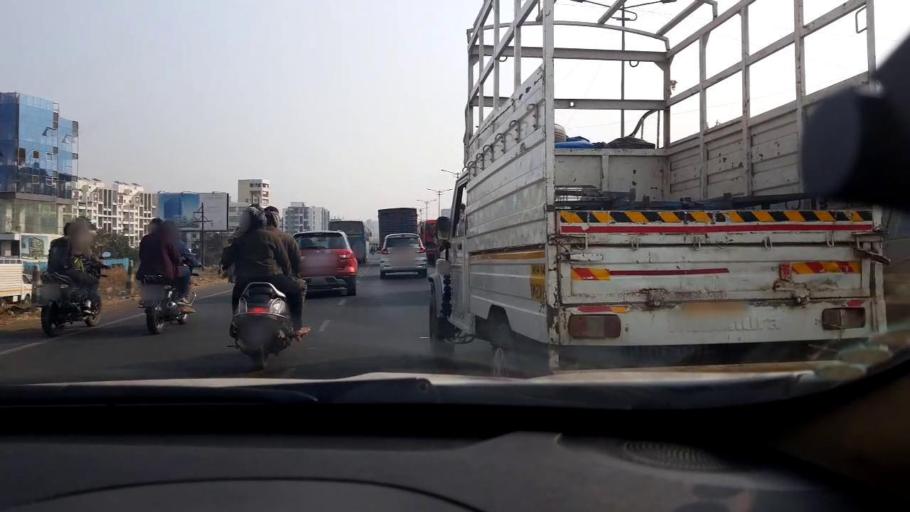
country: IN
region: Maharashtra
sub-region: Pune Division
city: Pimpri
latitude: 18.5644
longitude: 73.7676
